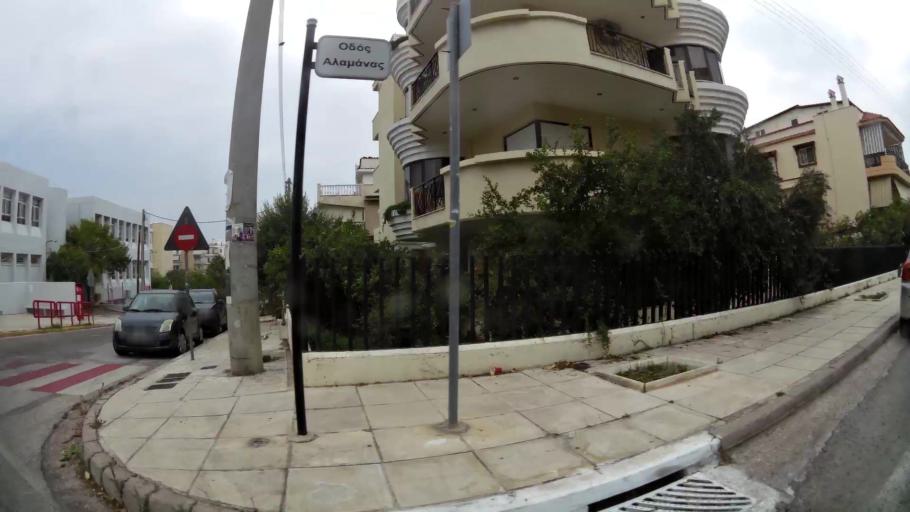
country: GR
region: Attica
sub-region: Nomarchia Athinas
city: Alimos
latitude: 37.9207
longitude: 23.7190
